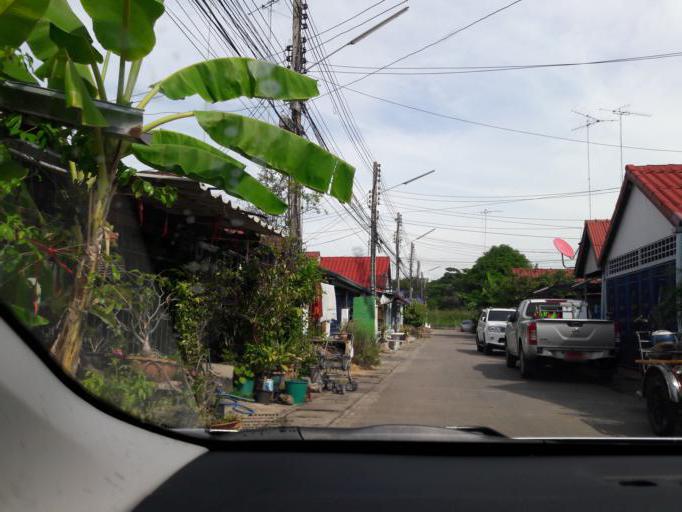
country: TH
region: Ang Thong
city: Ang Thong
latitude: 14.5853
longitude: 100.4400
